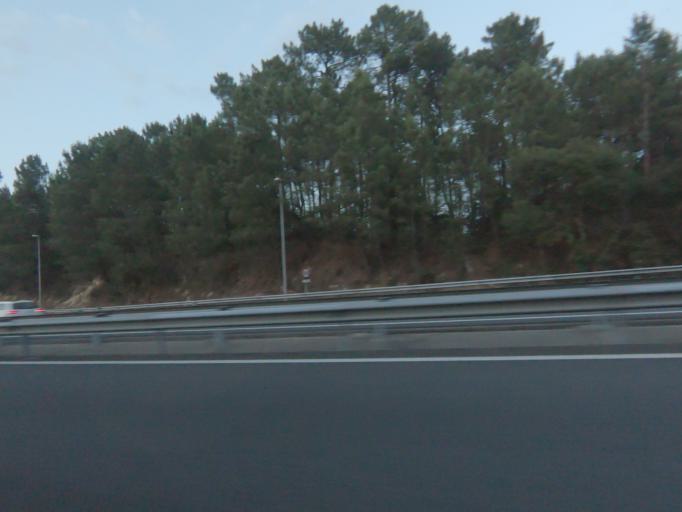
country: ES
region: Galicia
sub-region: Provincia de Pontevedra
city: Tui
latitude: 42.0921
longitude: -8.6270
